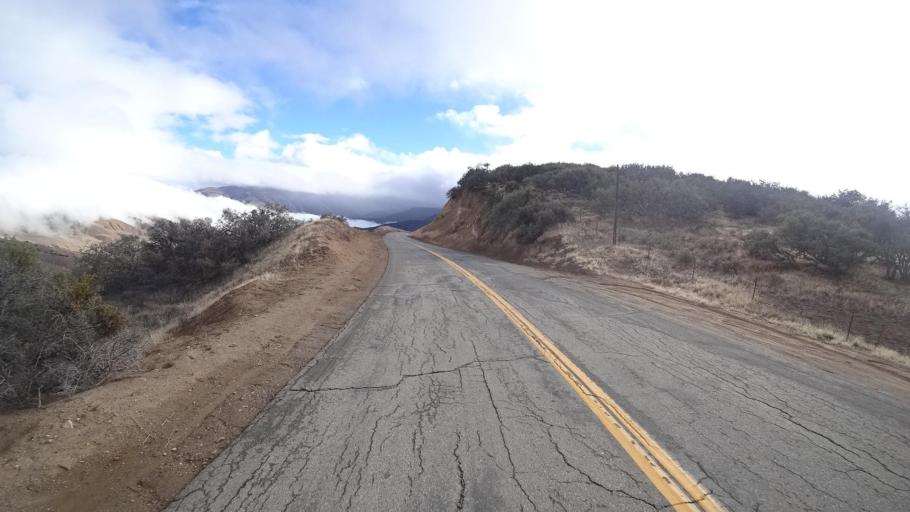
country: US
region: California
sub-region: Kern County
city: Maricopa
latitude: 34.8941
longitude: -119.3605
